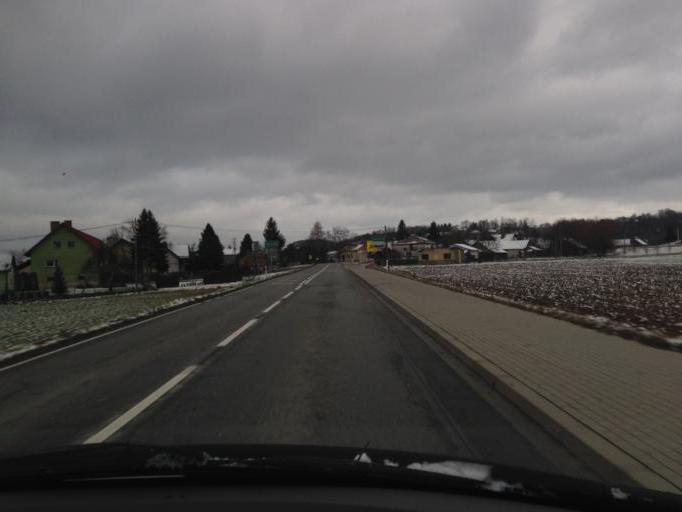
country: PL
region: Lesser Poland Voivodeship
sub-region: Powiat tarnowski
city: Zakliczyn
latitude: 49.8509
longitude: 20.8360
